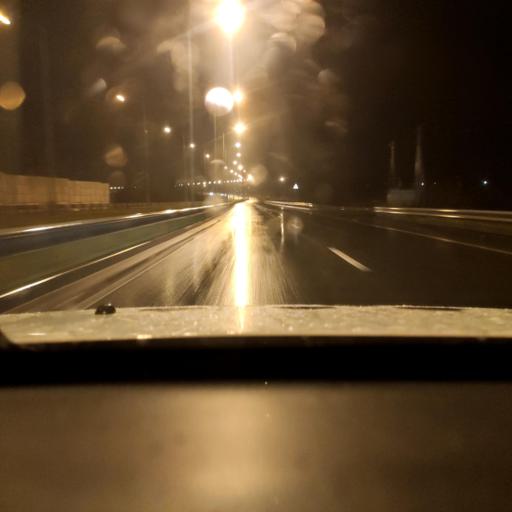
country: RU
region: Perm
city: Kondratovo
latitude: 57.9365
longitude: 56.0358
